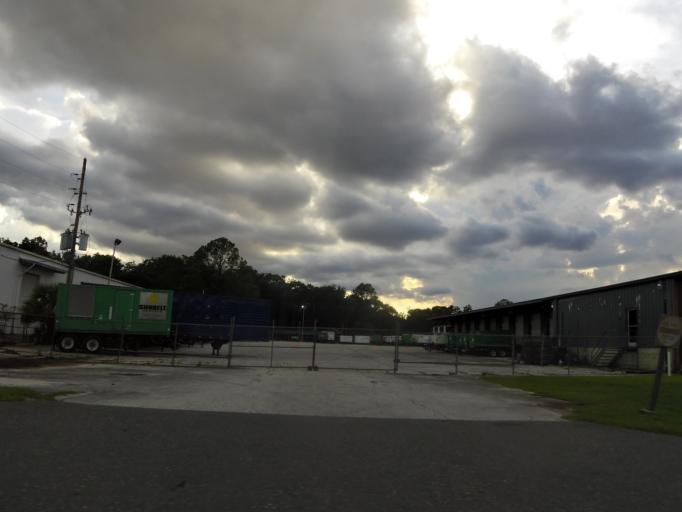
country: US
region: Florida
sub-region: Duval County
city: Jacksonville
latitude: 30.3195
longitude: -81.7646
